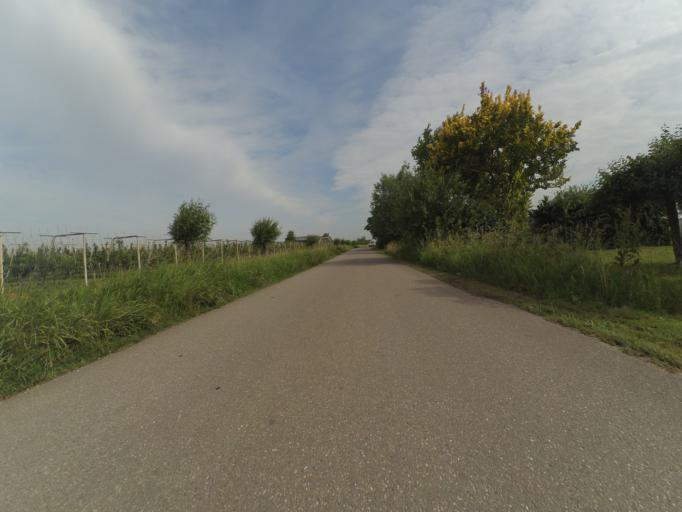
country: NL
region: Utrecht
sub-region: Gemeente Wijk bij Duurstede
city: Wijk bij Duurstede
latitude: 51.9430
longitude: 5.3448
